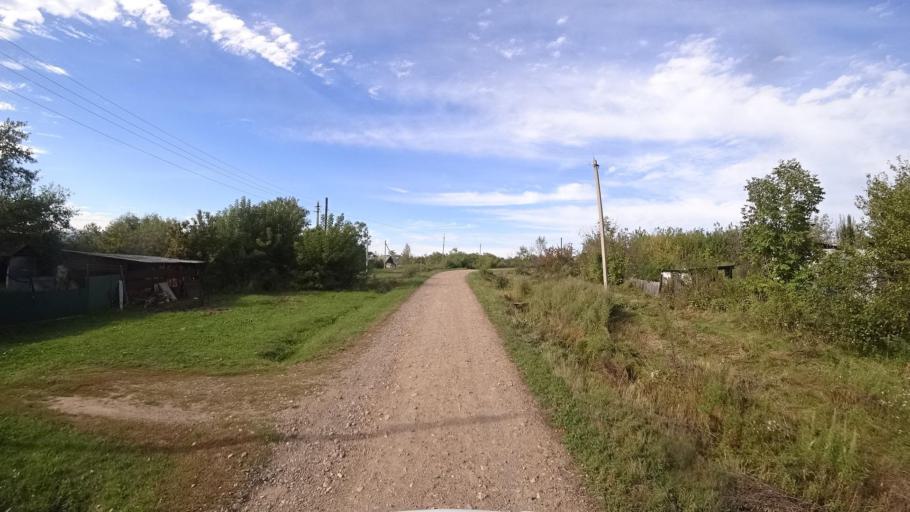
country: RU
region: Primorskiy
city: Dostoyevka
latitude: 44.2951
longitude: 133.4484
